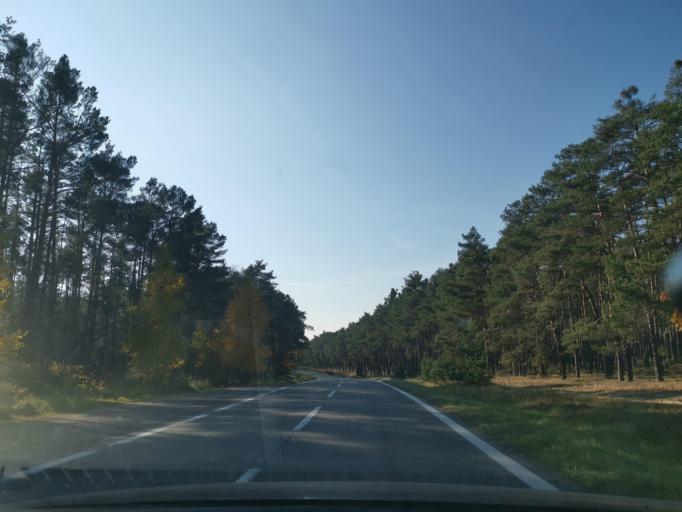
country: SK
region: Bratislavsky
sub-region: Okres Malacky
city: Malacky
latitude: 48.5039
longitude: 17.1136
